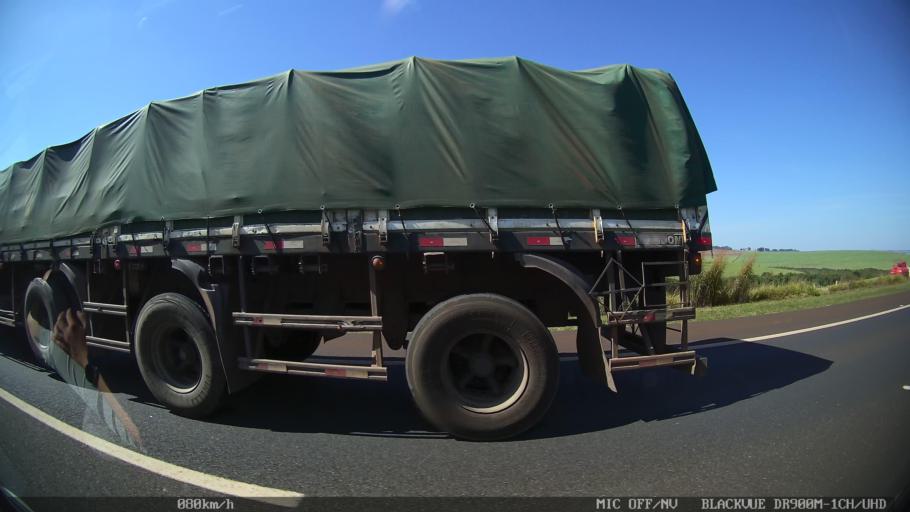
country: BR
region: Sao Paulo
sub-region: Franca
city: Franca
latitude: -20.7087
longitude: -47.5041
